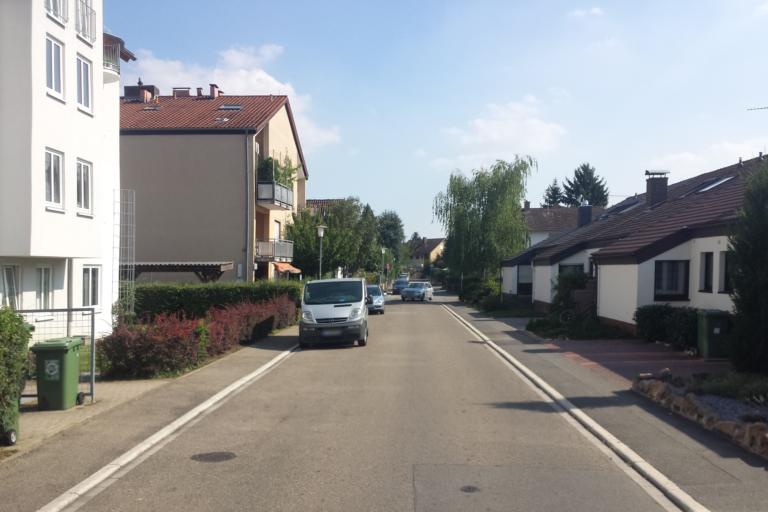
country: DE
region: Baden-Wuerttemberg
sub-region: Karlsruhe Region
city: Eppelheim
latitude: 49.4061
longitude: 8.6346
